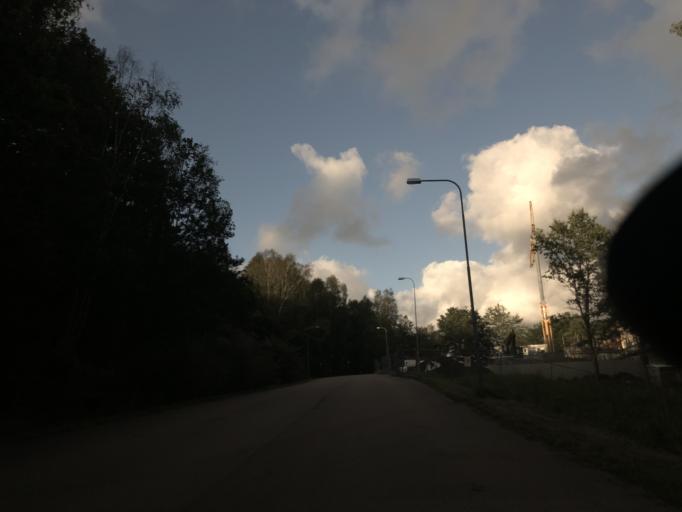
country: SE
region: Vaestra Goetaland
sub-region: Goteborg
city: Majorna
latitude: 57.7600
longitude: 11.9199
